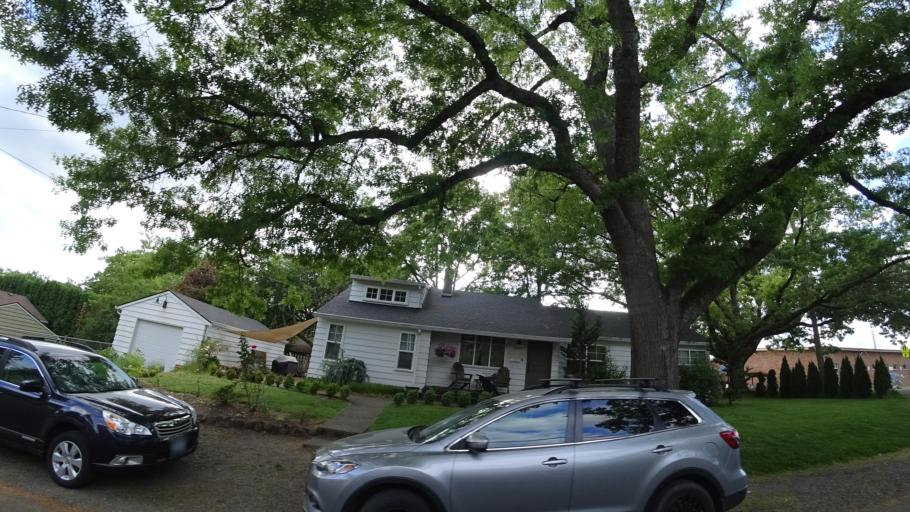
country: US
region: Oregon
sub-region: Washington County
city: Raleigh Hills
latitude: 45.4797
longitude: -122.7283
